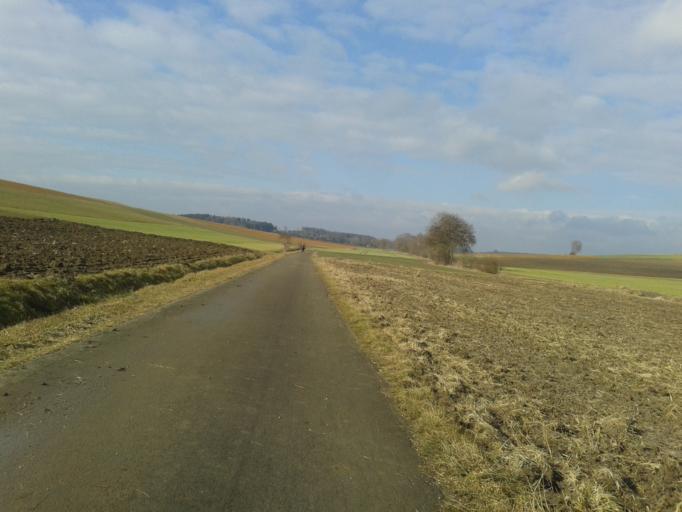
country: DE
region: Baden-Wuerttemberg
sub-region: Tuebingen Region
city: Oberdischingen
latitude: 48.3015
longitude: 9.8201
